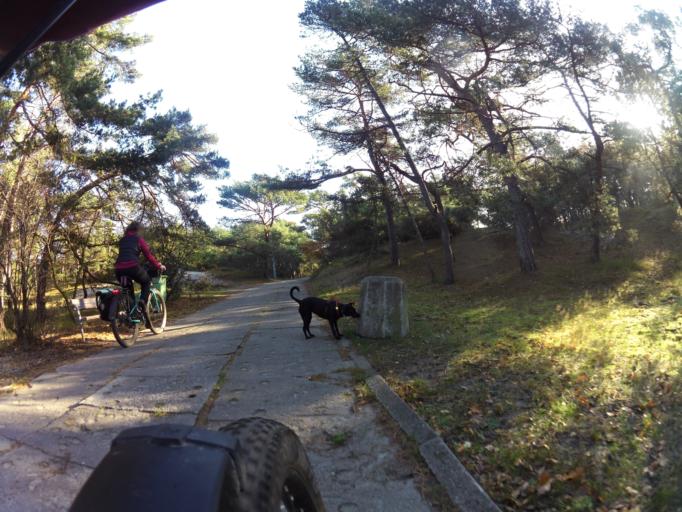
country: PL
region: Pomeranian Voivodeship
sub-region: Powiat pucki
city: Hel
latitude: 54.6026
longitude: 18.8137
